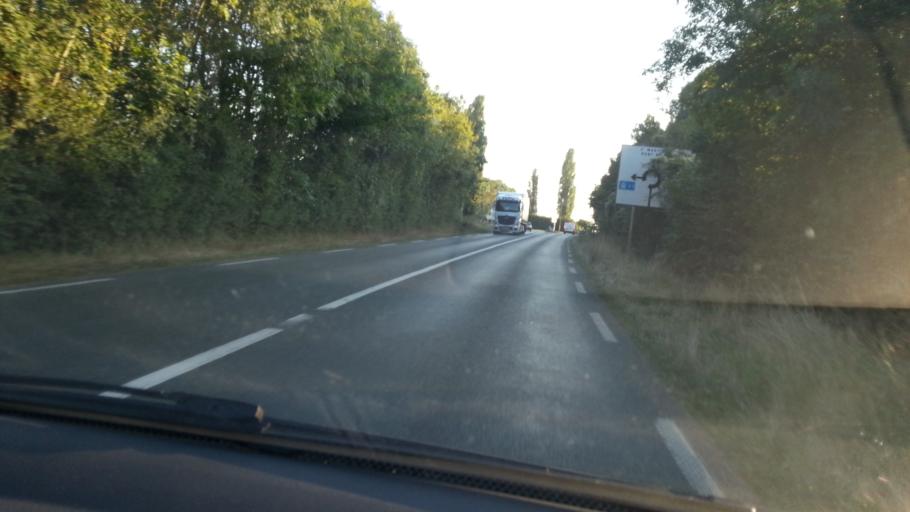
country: FR
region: Picardie
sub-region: Departement de l'Oise
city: Estrees-Saint-Denis
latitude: 49.4057
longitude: 2.6269
